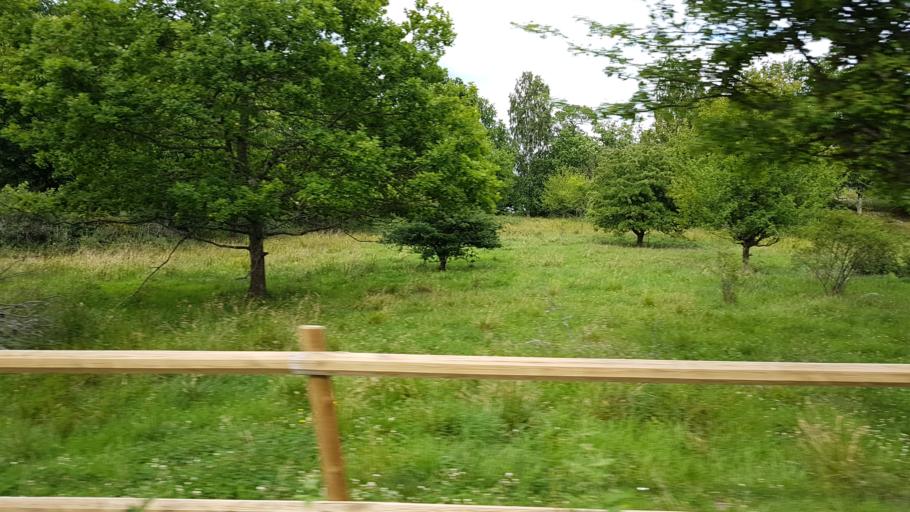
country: SE
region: OEstergoetland
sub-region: Valdemarsviks Kommun
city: Gusum
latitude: 58.4354
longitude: 16.5991
